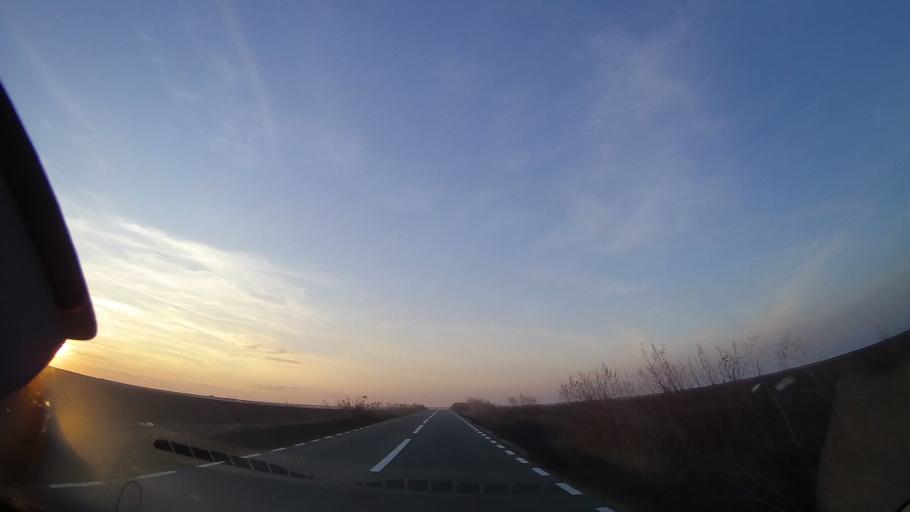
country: RO
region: Constanta
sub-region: Comuna Topraisar
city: Topraisar
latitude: 44.0226
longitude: 28.4108
